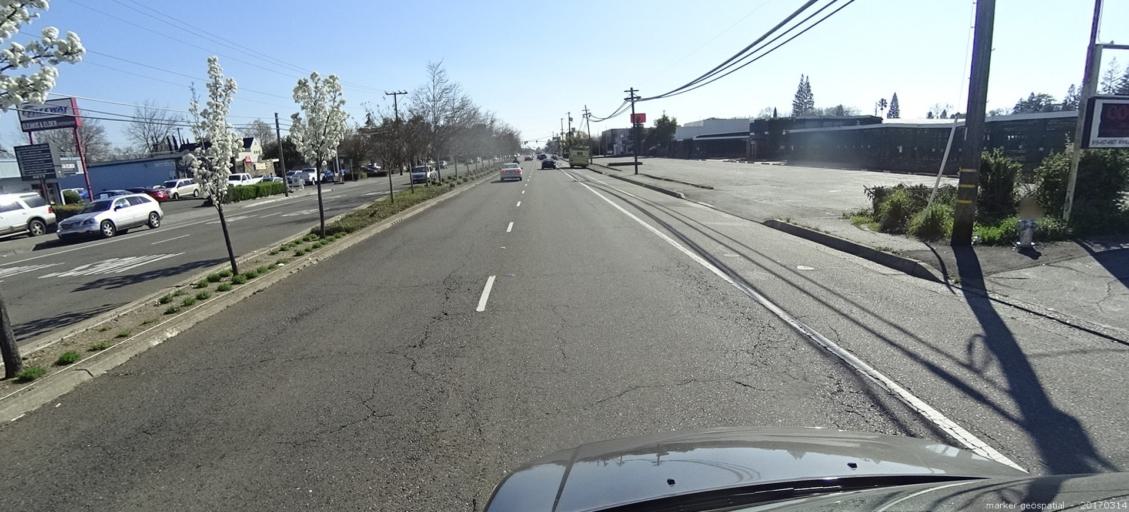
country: US
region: California
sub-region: Sacramento County
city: Sacramento
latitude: 38.5336
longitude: -121.4944
